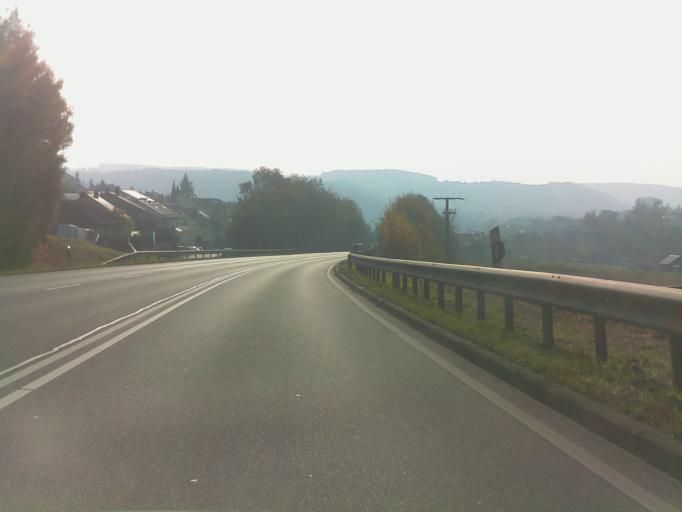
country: DE
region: Baden-Wuerttemberg
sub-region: Karlsruhe Region
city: Mosbach
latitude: 49.3916
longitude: 9.1974
